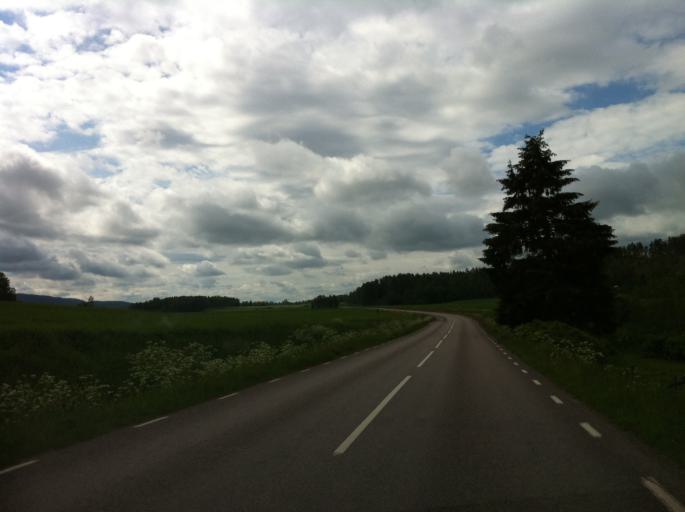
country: SE
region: Vaermland
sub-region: Sunne Kommun
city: Sunne
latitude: 59.9014
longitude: 13.1717
